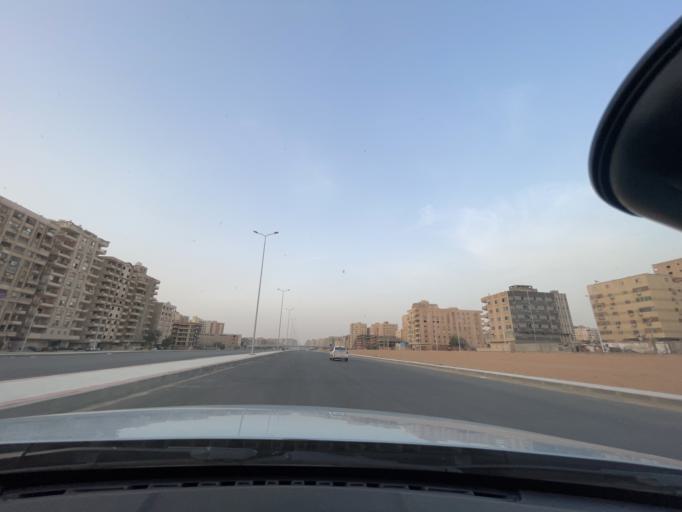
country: EG
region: Muhafazat al Qahirah
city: Cairo
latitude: 30.0534
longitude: 31.3713
